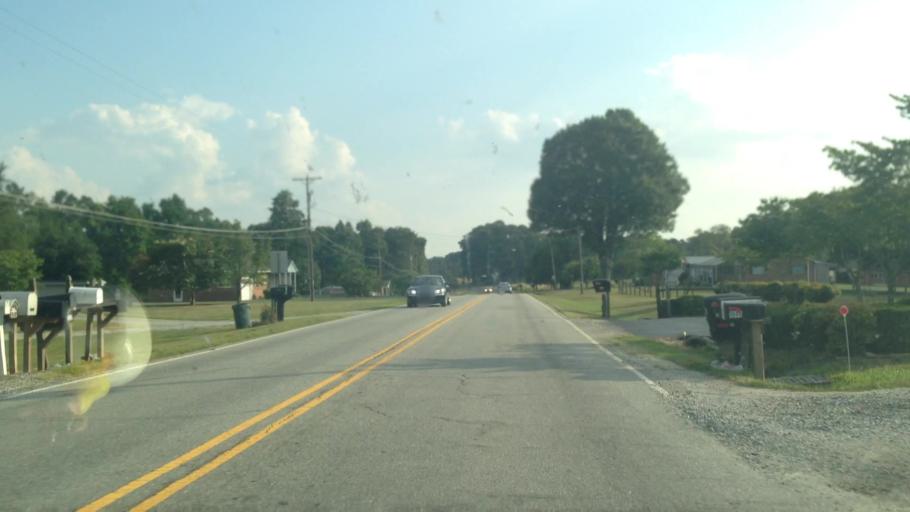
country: US
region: North Carolina
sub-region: Forsyth County
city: Kernersville
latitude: 36.0677
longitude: -80.0604
